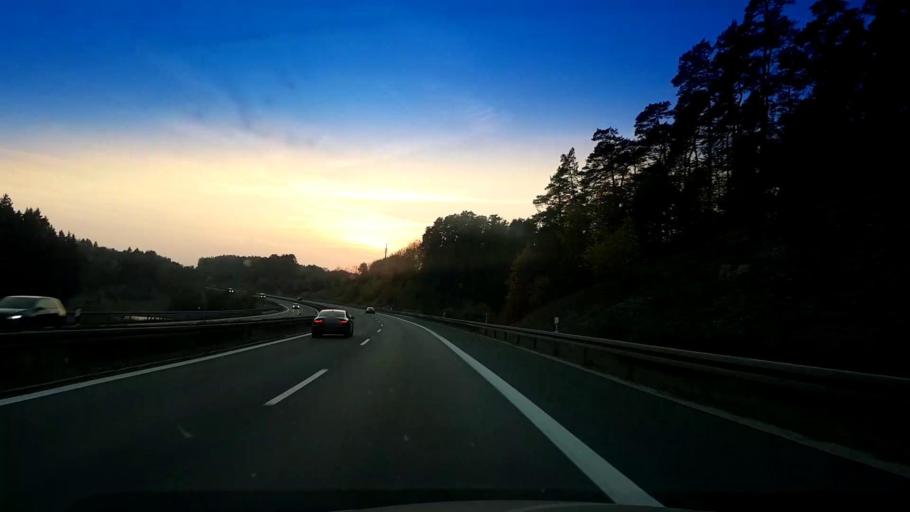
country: DE
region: Bavaria
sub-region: Upper Franconia
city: Wonsees
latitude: 50.0103
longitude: 11.3078
